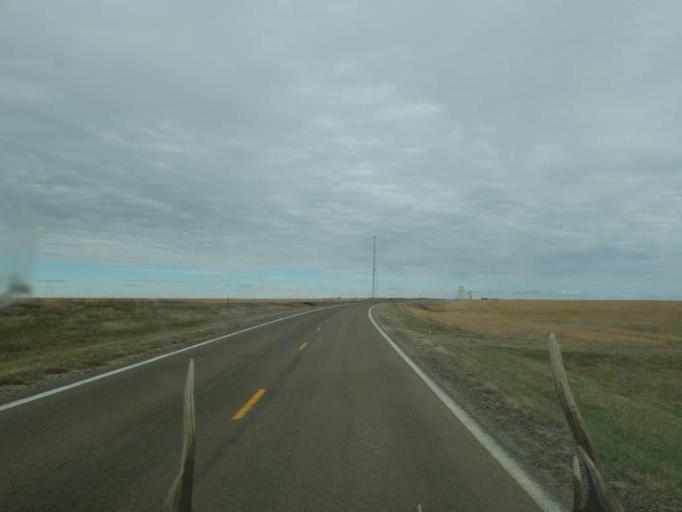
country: US
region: Kansas
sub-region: Thomas County
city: Colby
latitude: 39.0492
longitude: -101.2652
